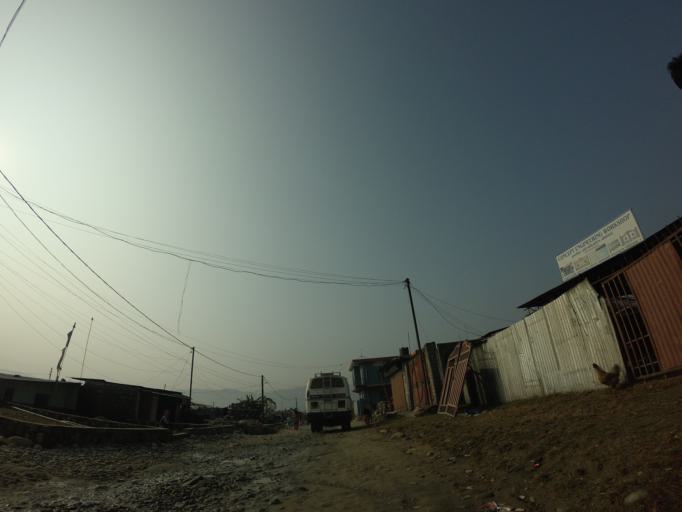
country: NP
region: Western Region
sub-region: Gandaki Zone
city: Pokhara
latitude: 28.2049
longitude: 83.9869
